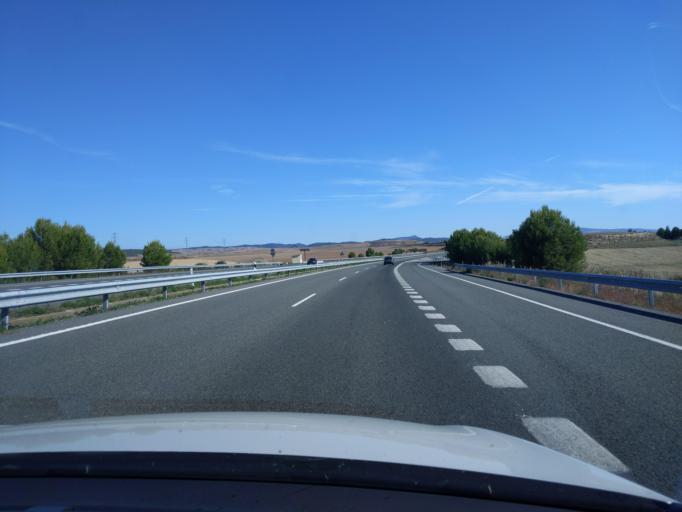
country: ES
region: Navarre
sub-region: Provincia de Navarra
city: Los Arcos
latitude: 42.5379
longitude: -2.2155
